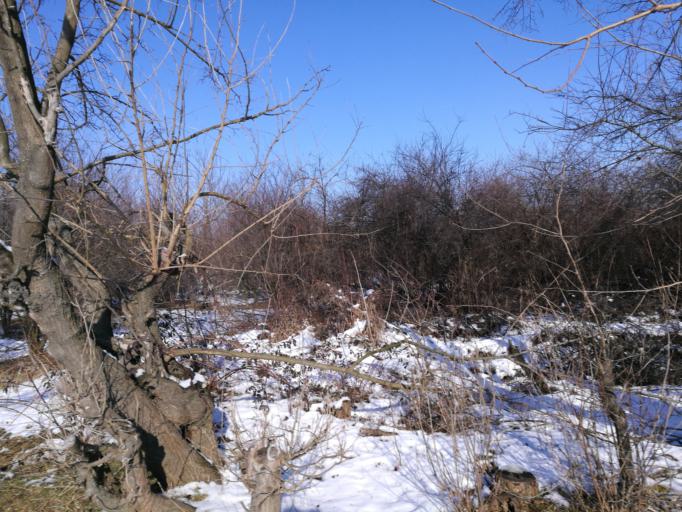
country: RO
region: Ilfov
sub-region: Comuna Otopeni
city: Otopeni
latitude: 44.5031
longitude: 26.0666
